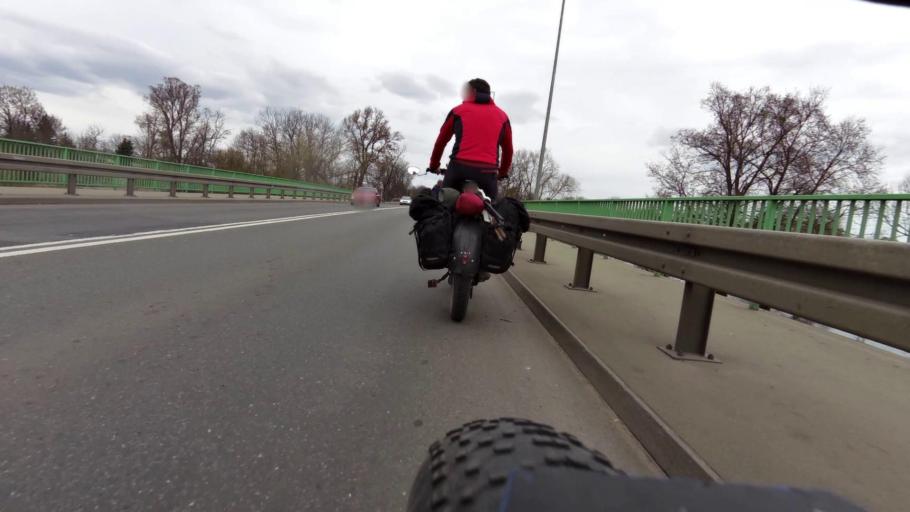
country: PL
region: Lubusz
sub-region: Powiat gorzowski
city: Kostrzyn nad Odra
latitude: 52.5817
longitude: 14.6436
